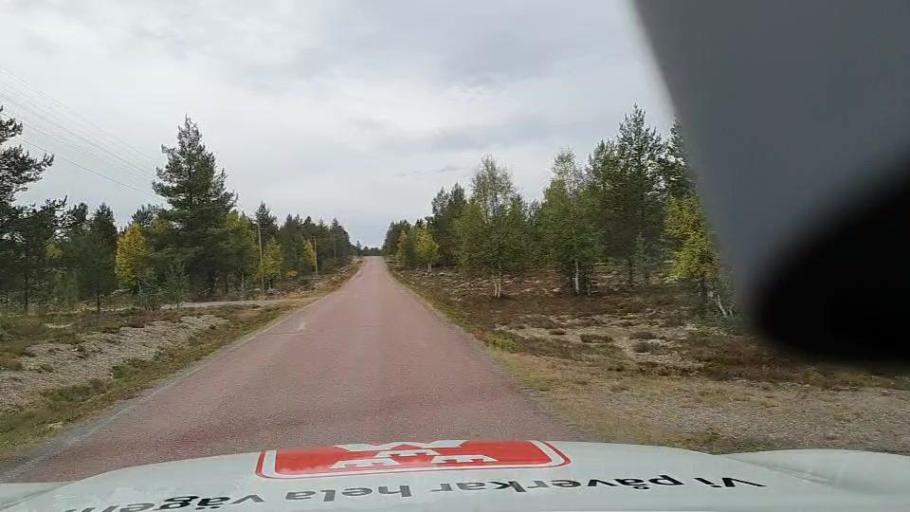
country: NO
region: Hedmark
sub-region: Engerdal
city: Engerdal
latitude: 62.0570
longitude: 12.7402
